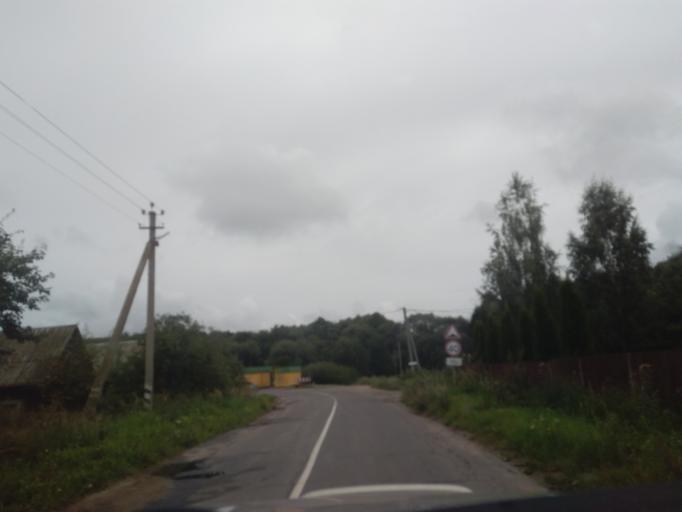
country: BY
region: Minsk
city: Zhdanovichy
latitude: 53.9288
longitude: 27.3838
